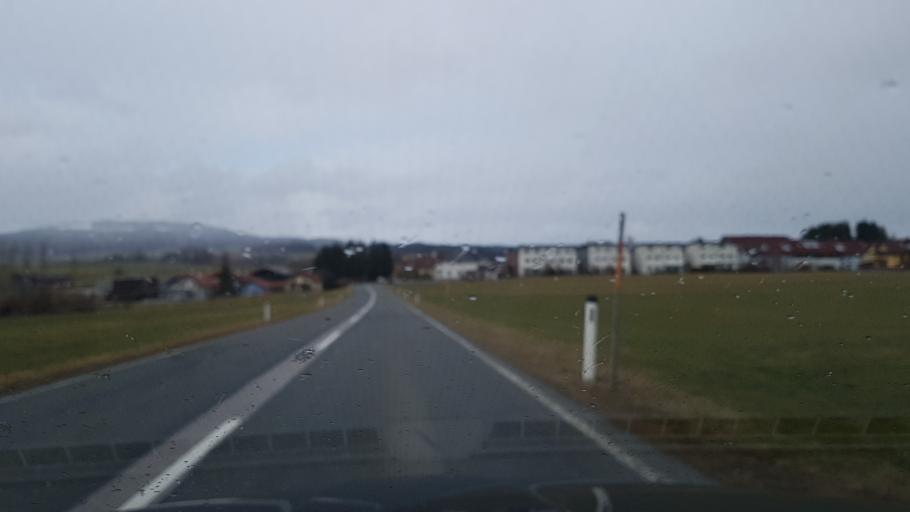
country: AT
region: Salzburg
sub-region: Politischer Bezirk Salzburg-Umgebung
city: Neumarkt am Wallersee
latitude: 47.9294
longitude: 13.2210
